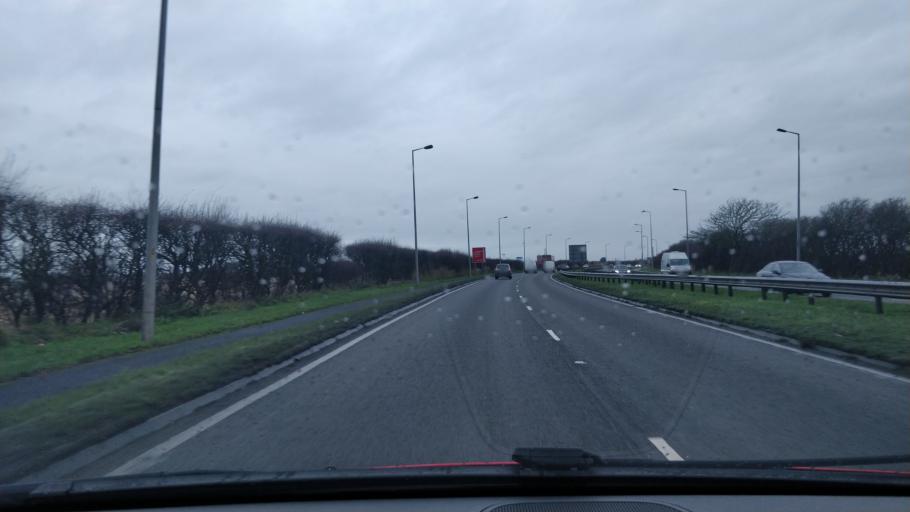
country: GB
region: England
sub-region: Sefton
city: Hightown
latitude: 53.5388
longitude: -3.0469
